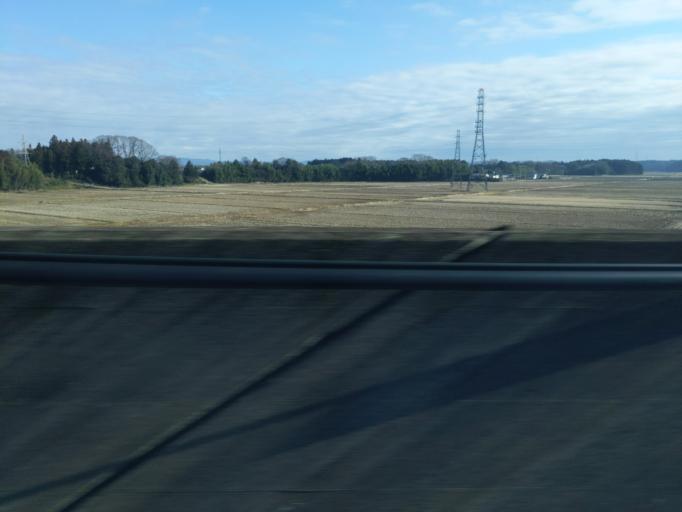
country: JP
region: Tochigi
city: Yaita
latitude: 36.8314
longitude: 139.9614
